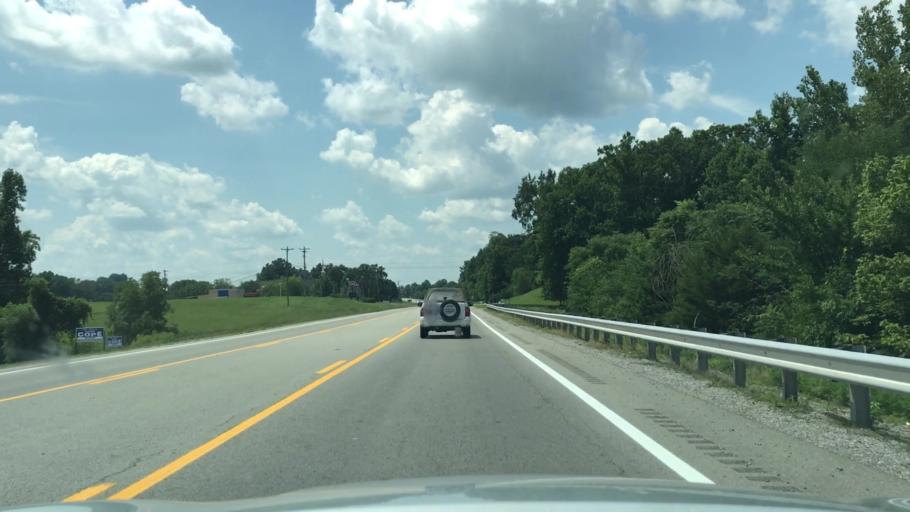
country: US
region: Tennessee
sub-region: Pickett County
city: Byrdstown
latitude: 36.5630
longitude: -85.1663
